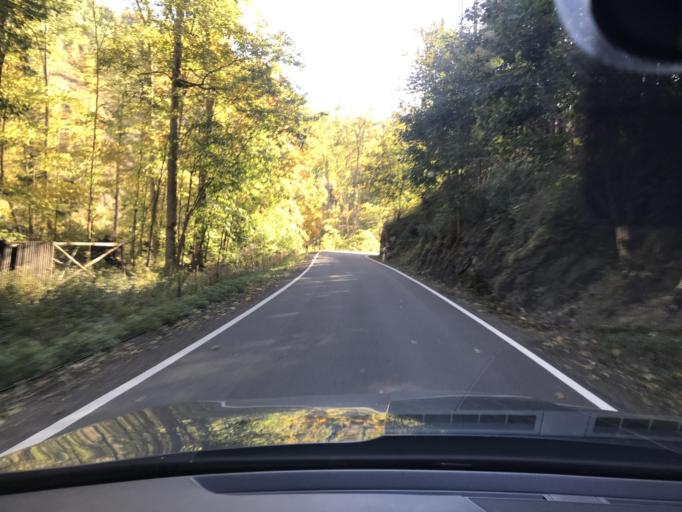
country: DE
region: Saxony-Anhalt
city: Friedrichsbrunn
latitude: 51.6988
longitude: 10.9672
